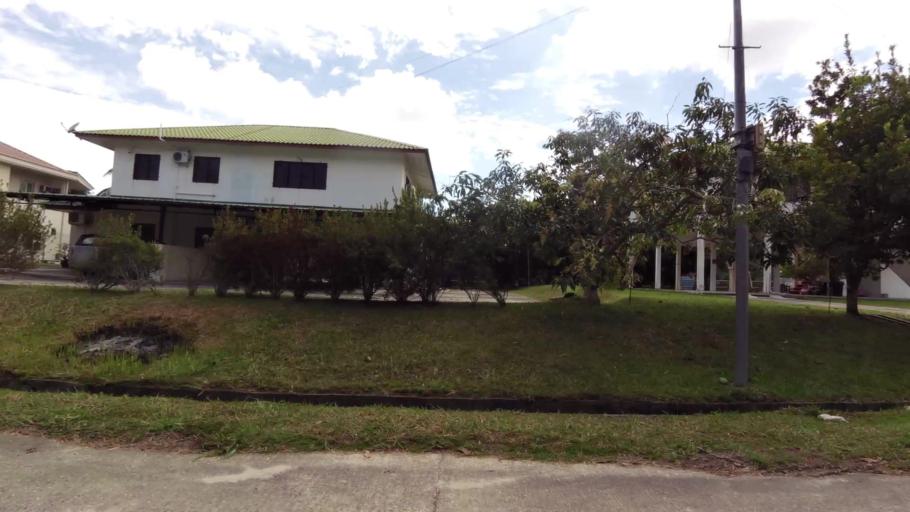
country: BN
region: Brunei and Muara
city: Bandar Seri Begawan
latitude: 4.9354
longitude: 114.8943
